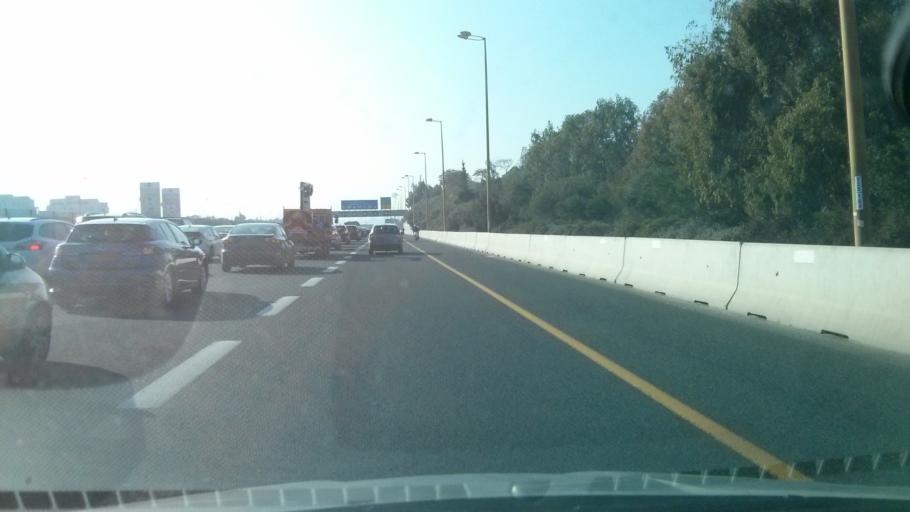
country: IL
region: Tel Aviv
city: Ramat HaSharon
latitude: 32.1289
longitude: 34.8098
